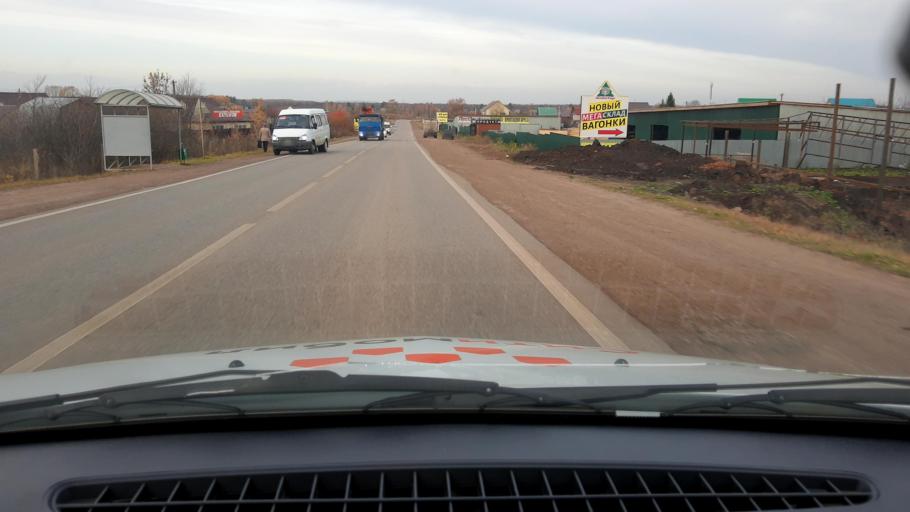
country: RU
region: Bashkortostan
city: Kabakovo
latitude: 54.7173
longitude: 56.1724
